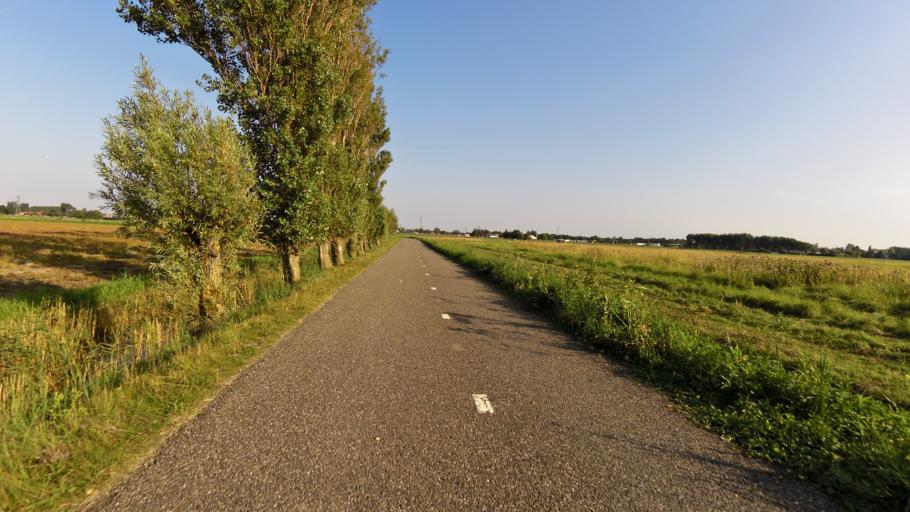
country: NL
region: South Holland
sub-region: Gemeente Teylingen
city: Voorhout
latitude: 52.2052
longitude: 4.4674
